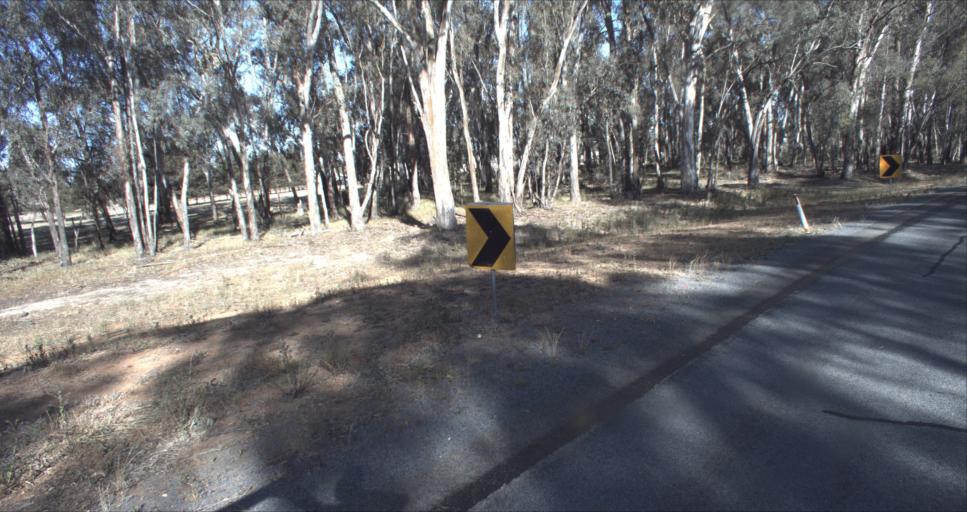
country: AU
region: New South Wales
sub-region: Leeton
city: Leeton
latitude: -34.6334
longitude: 146.3756
